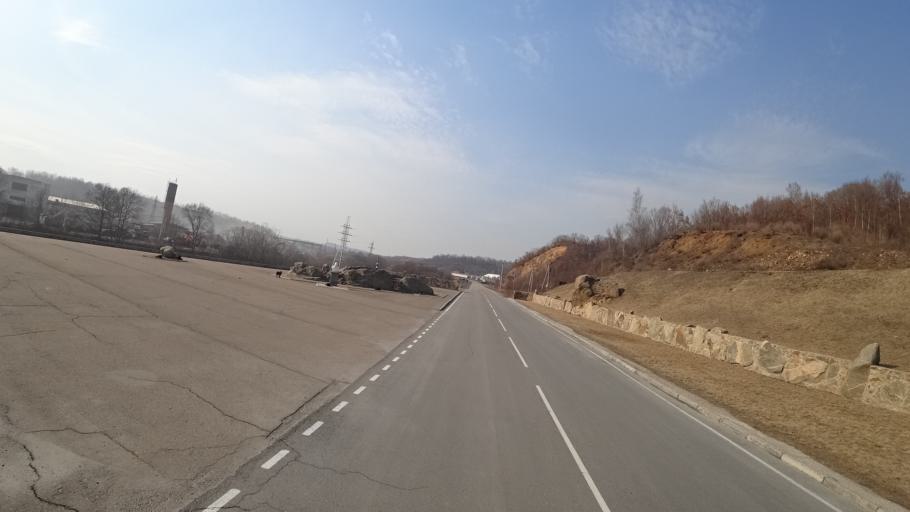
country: RU
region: Amur
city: Novobureyskiy
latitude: 49.7900
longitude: 129.9656
